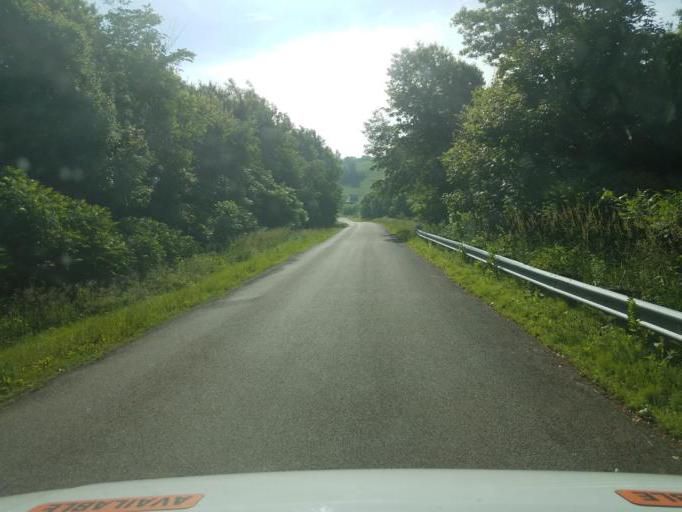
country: US
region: Wisconsin
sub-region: Sauk County
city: Reedsburg
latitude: 43.5802
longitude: -90.1517
